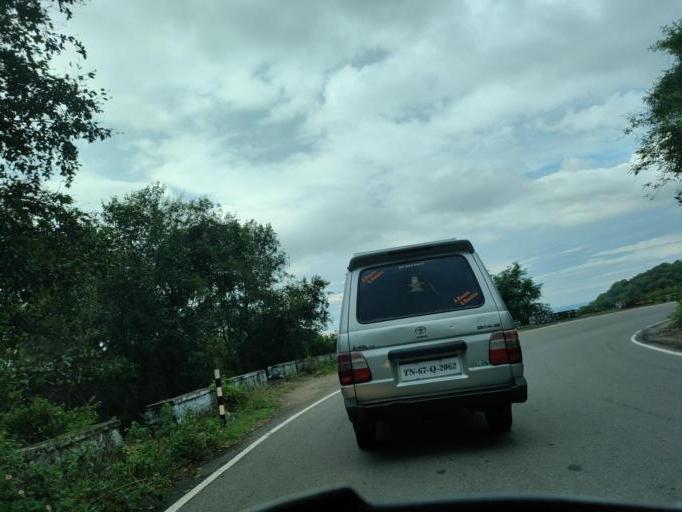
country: IN
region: Tamil Nadu
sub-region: Dindigul
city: Palani
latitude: 10.3654
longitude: 77.5257
